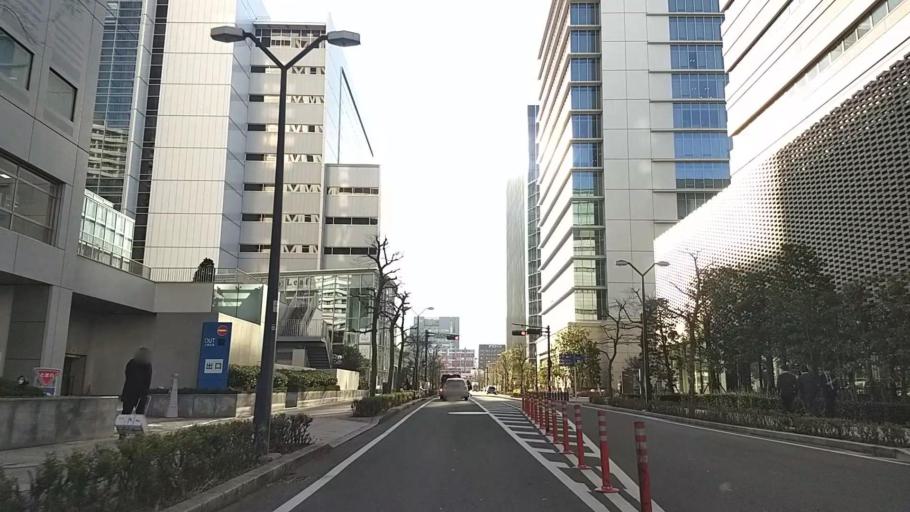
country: JP
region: Kanagawa
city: Yokohama
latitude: 35.4602
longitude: 139.6299
